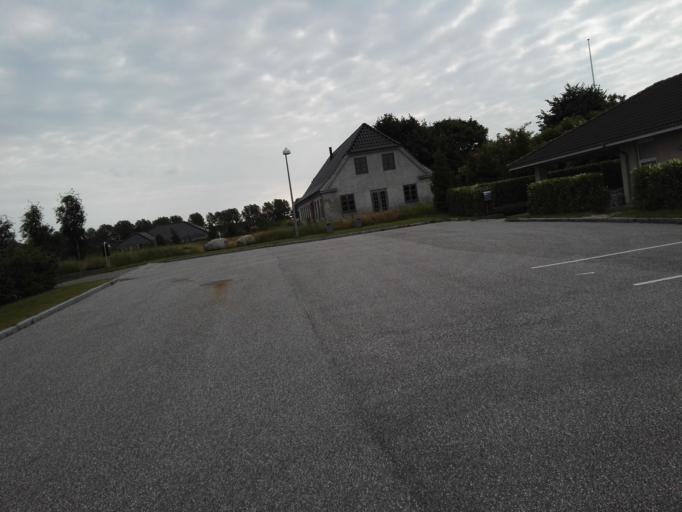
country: DK
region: Capital Region
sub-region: Egedal Kommune
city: Olstykke
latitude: 55.7870
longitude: 12.1487
